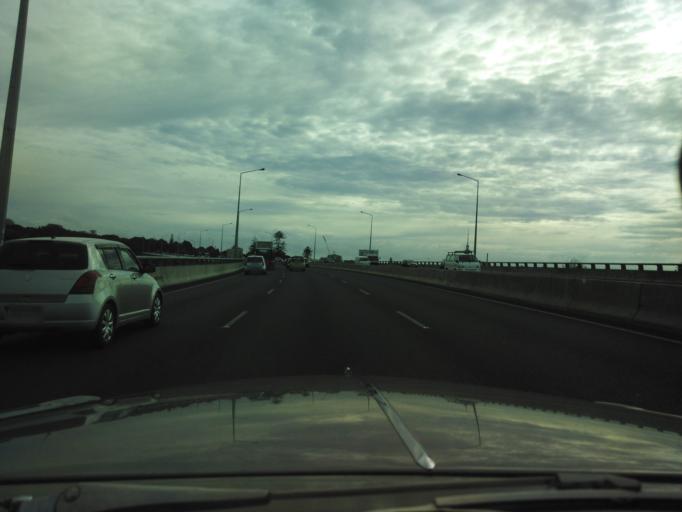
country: NZ
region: Auckland
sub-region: Auckland
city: Auckland
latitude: -36.8754
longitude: 174.7802
